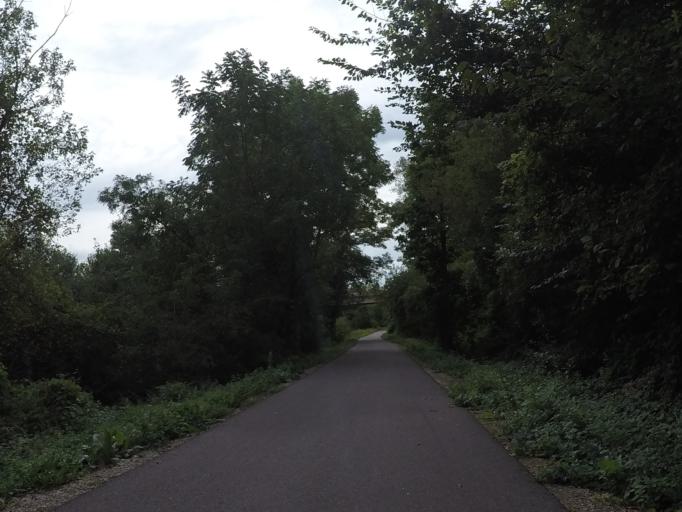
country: US
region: Wisconsin
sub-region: Sauk County
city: Prairie du Sac
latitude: 43.2945
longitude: -89.7240
